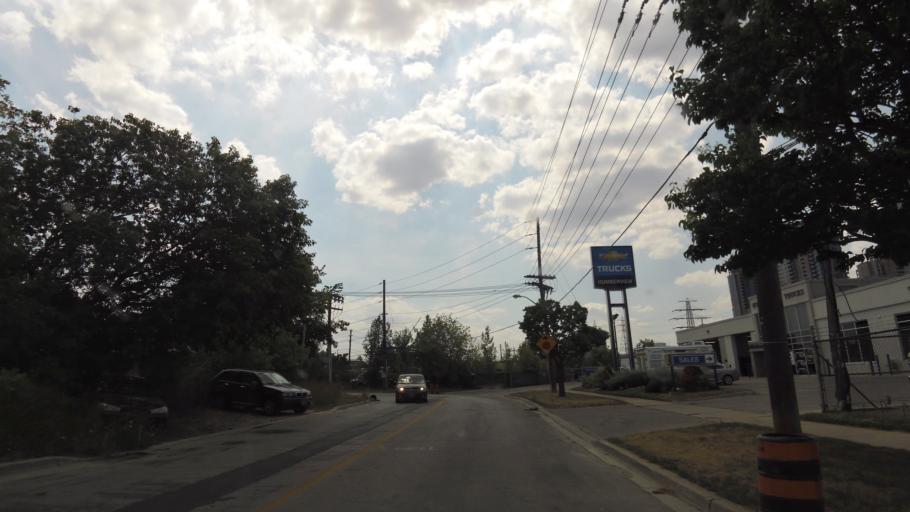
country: CA
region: Ontario
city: Etobicoke
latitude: 43.6394
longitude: -79.5311
